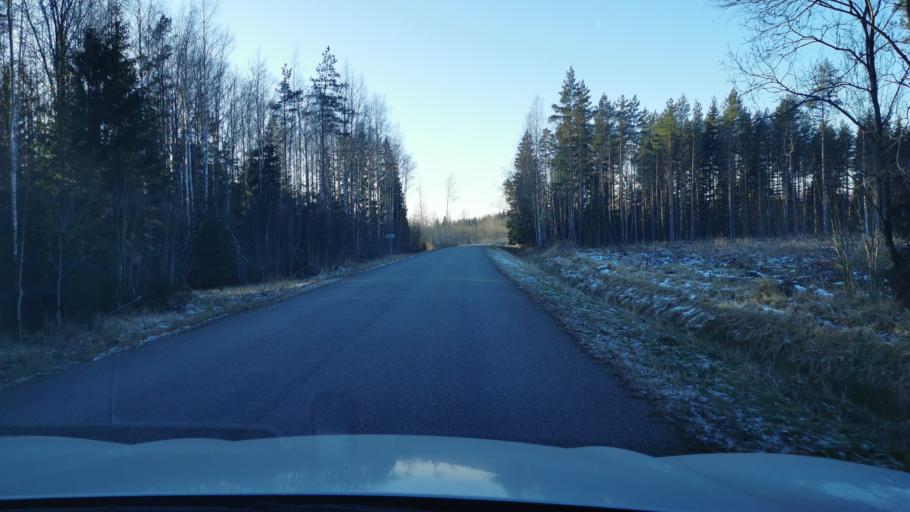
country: EE
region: Ida-Virumaa
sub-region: Kivioli linn
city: Kivioli
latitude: 59.2161
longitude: 26.9441
